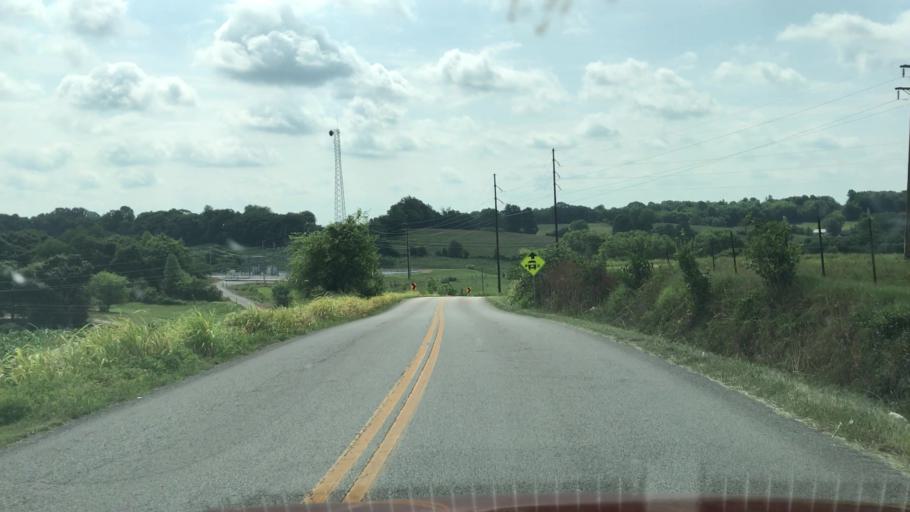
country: US
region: Kentucky
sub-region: Barren County
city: Glasgow
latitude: 36.9725
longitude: -85.8950
